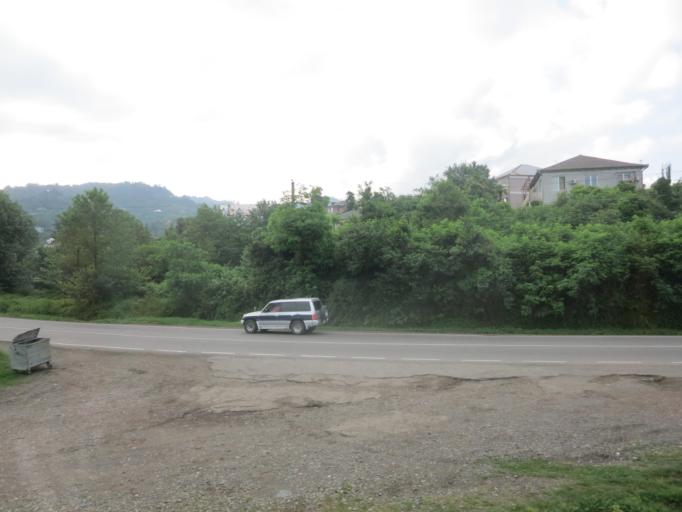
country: GE
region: Ajaria
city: Makhinjauri
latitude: 41.6858
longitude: 41.7019
